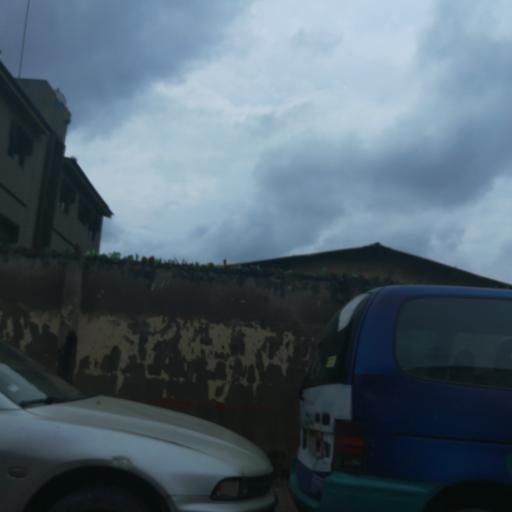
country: NG
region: Lagos
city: Ojota
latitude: 6.5888
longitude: 3.3843
